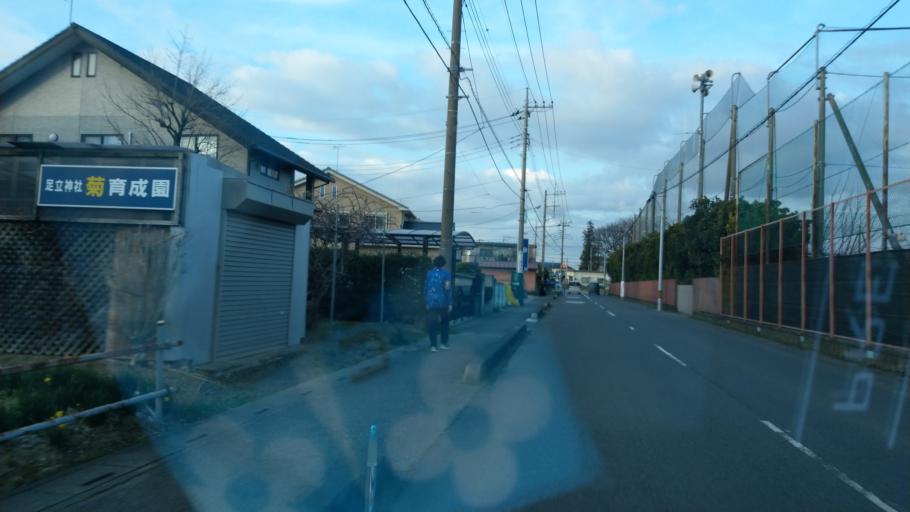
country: JP
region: Saitama
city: Yono
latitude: 35.8953
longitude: 139.5878
